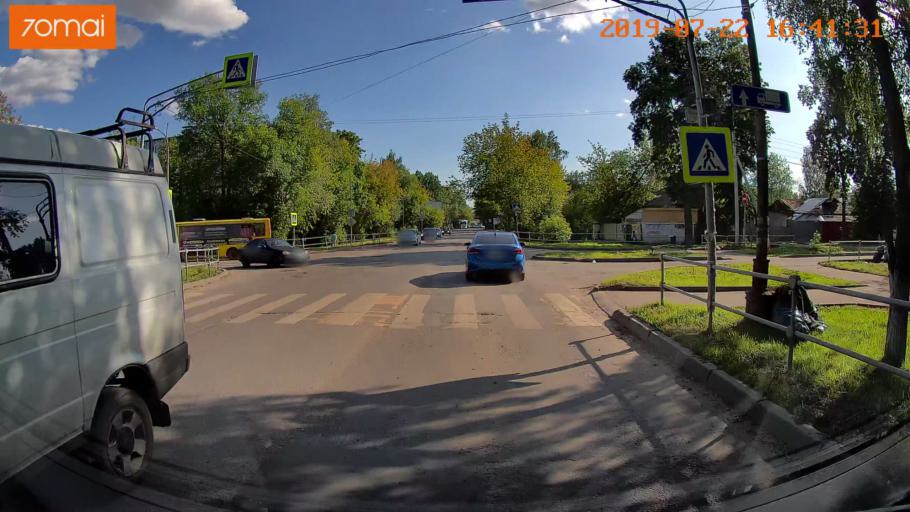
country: RU
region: Ivanovo
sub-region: Gorod Ivanovo
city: Ivanovo
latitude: 57.0210
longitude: 40.9602
